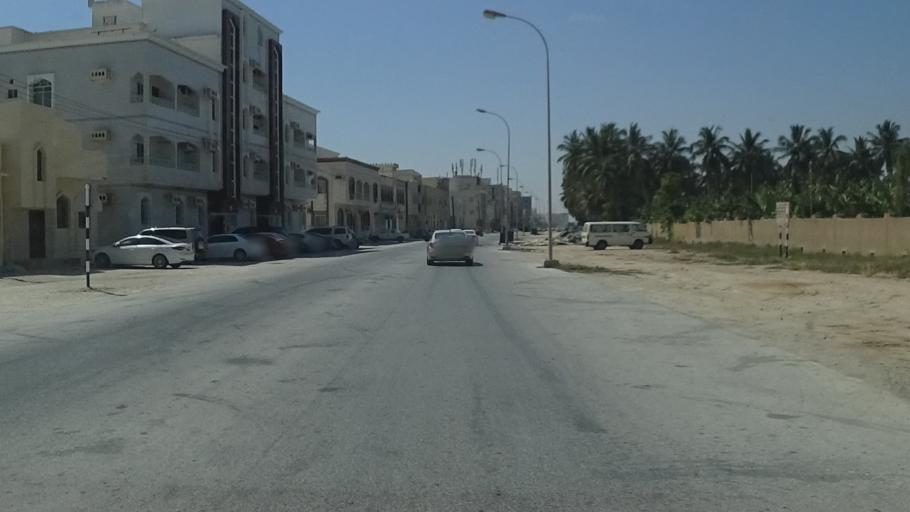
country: OM
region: Zufar
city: Salalah
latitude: 17.0223
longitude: 54.1247
